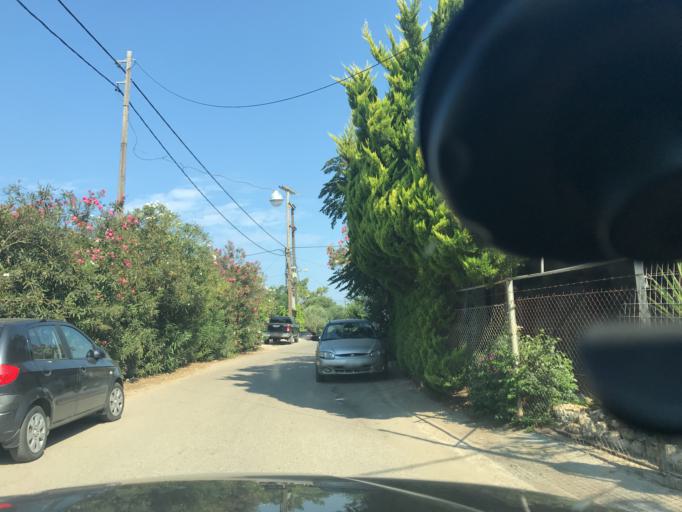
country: GR
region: West Greece
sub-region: Nomos Ileias
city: Kardamas
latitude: 37.7198
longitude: 21.3121
